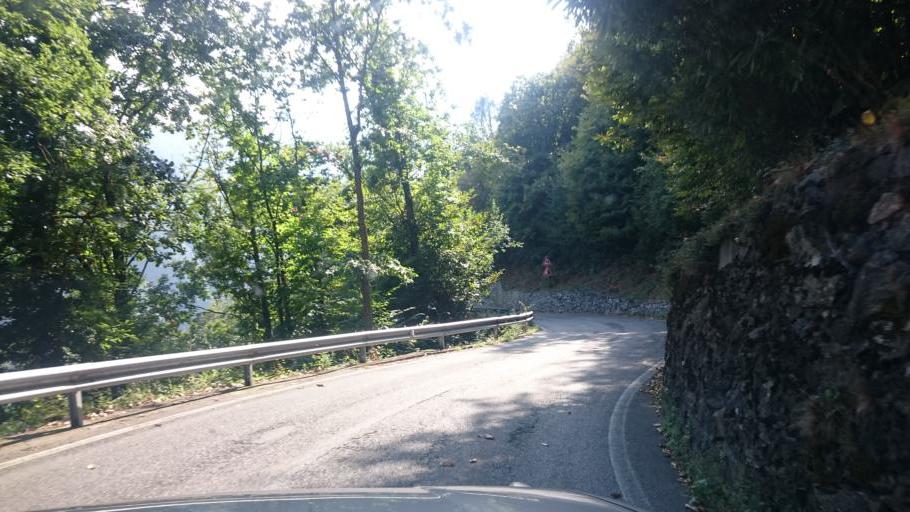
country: IT
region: Lombardy
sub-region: Provincia di Brescia
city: Paisco Loveno
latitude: 46.0889
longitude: 10.3060
